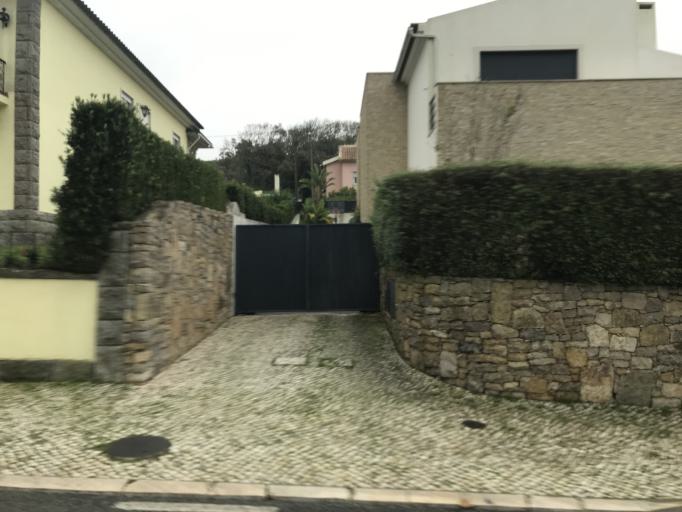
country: PT
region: Lisbon
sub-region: Sintra
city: Sintra
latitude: 38.7908
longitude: -9.3738
